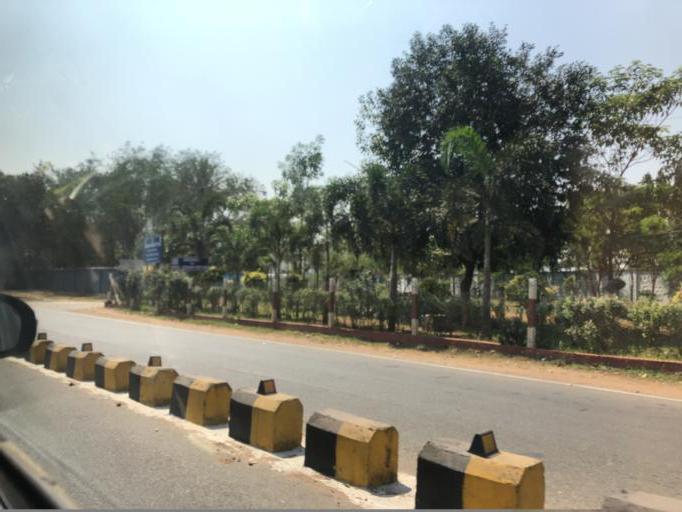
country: IN
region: Andhra Pradesh
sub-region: Vishakhapatnam
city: Yarada
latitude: 17.6953
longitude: 83.2685
